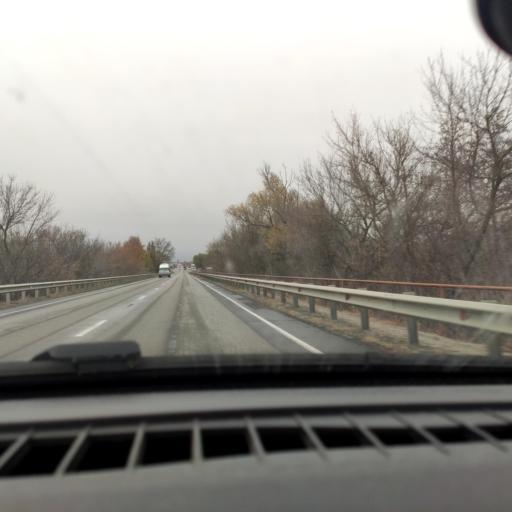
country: RU
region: Voronezj
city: Uryv-Pokrovka
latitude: 51.0398
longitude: 38.9836
